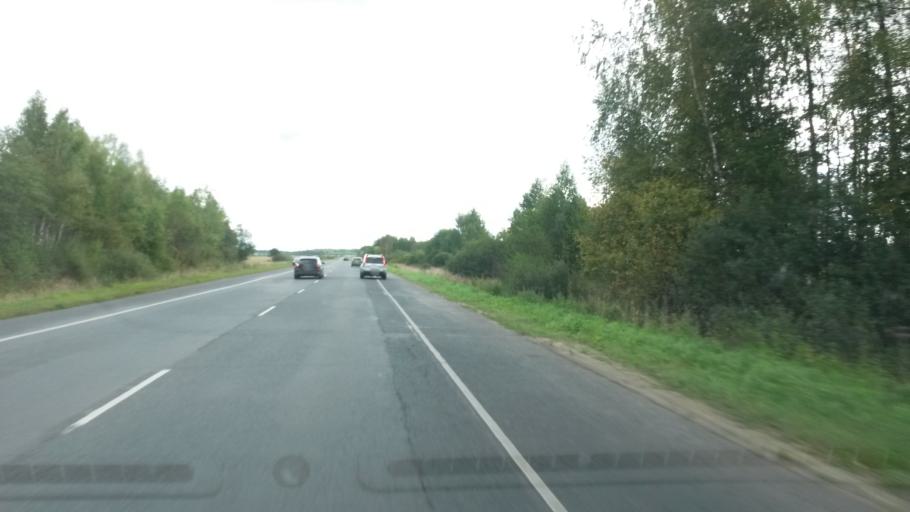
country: RU
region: Ivanovo
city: Rodniki
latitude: 57.0871
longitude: 41.6304
